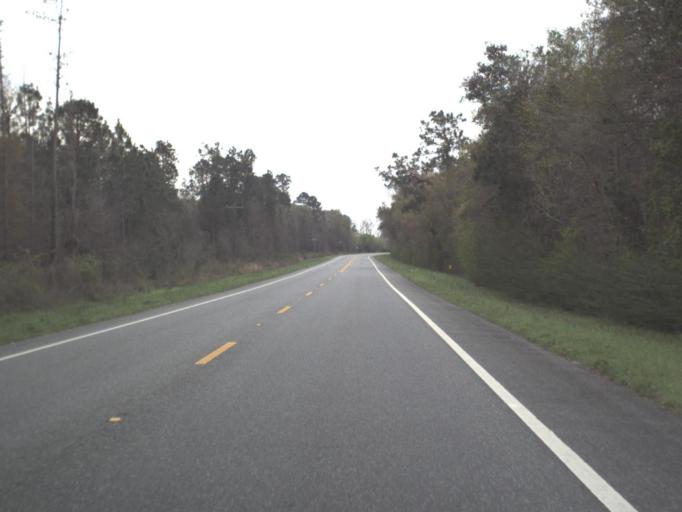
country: US
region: Florida
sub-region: Calhoun County
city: Blountstown
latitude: 30.4741
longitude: -85.1994
